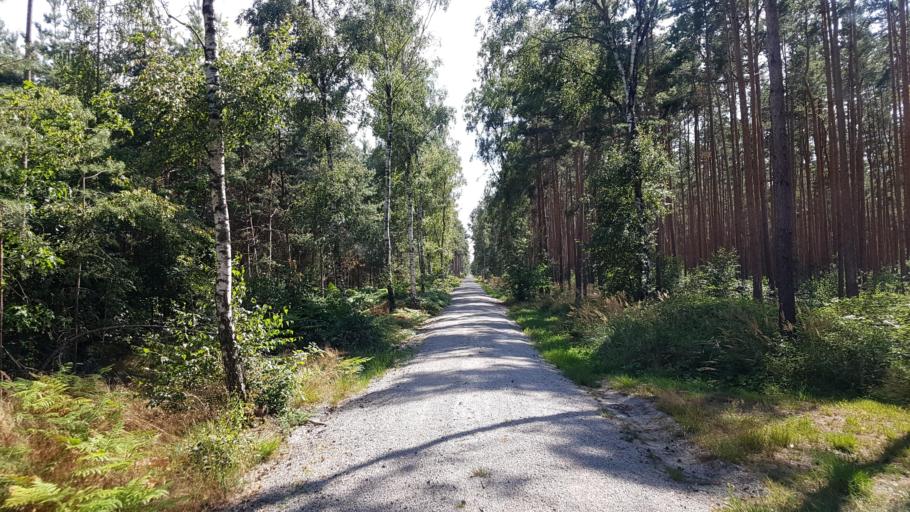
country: DE
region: Brandenburg
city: Bad Liebenwerda
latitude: 51.4867
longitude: 13.3110
